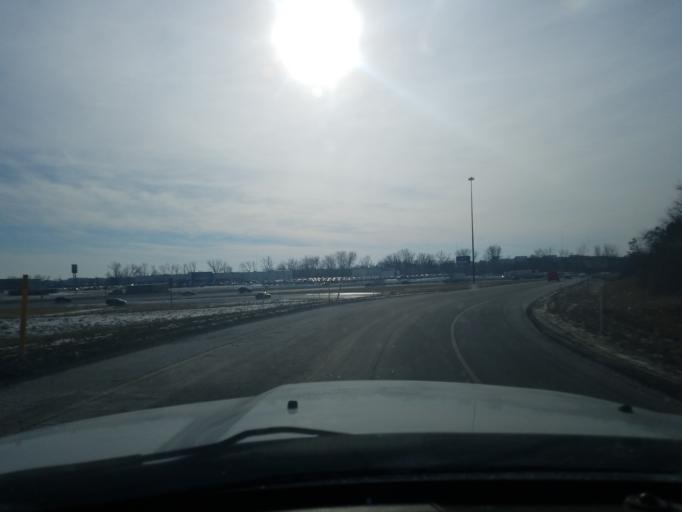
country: US
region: Indiana
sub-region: Allen County
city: Fort Wayne
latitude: 41.1313
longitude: -85.1602
